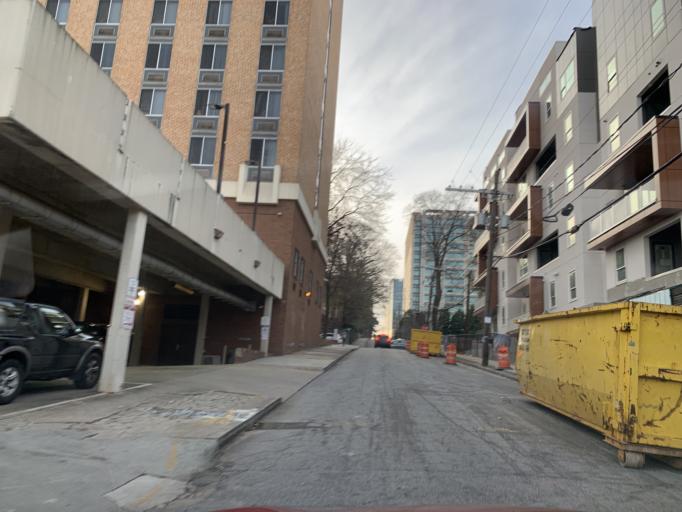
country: US
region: Georgia
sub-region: Fulton County
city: Atlanta
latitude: 33.7748
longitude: -84.3822
